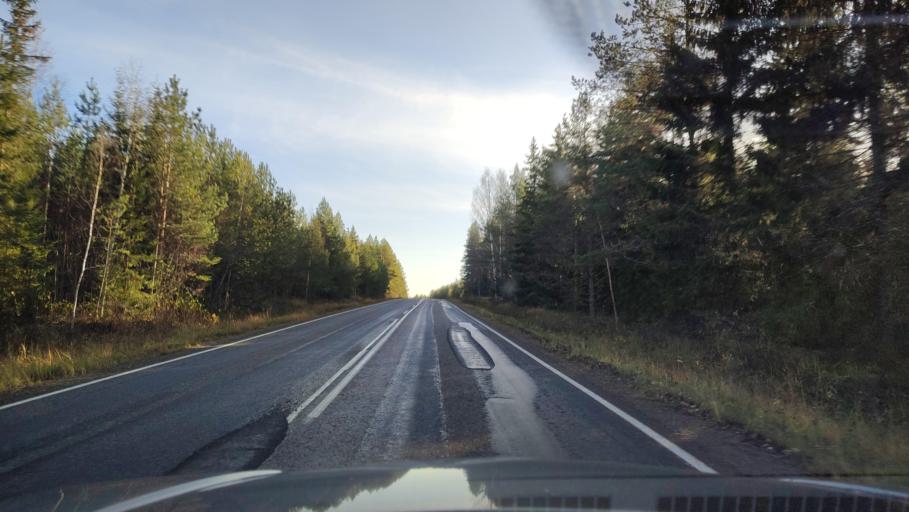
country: FI
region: Southern Ostrobothnia
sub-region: Suupohja
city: Karijoki
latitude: 62.2351
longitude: 21.7020
